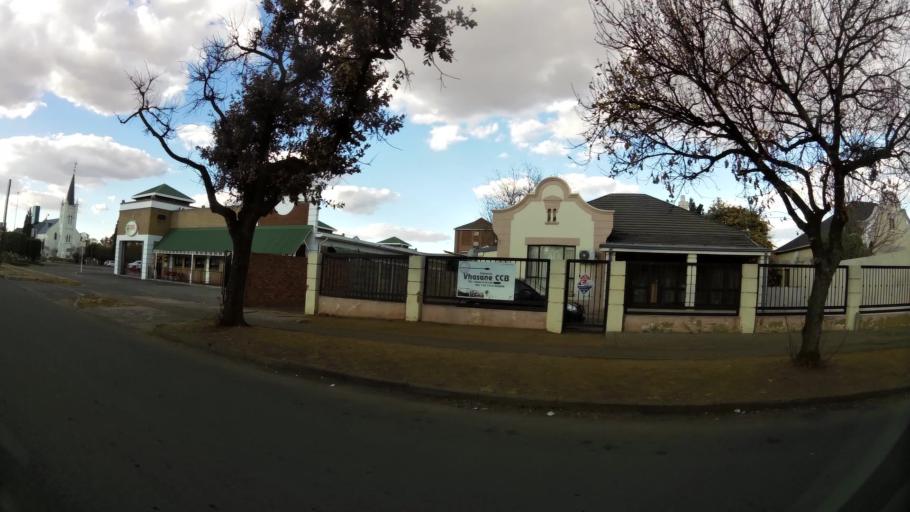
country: ZA
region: North-West
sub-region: Dr Kenneth Kaunda District Municipality
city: Potchefstroom
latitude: -26.7149
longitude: 27.0909
